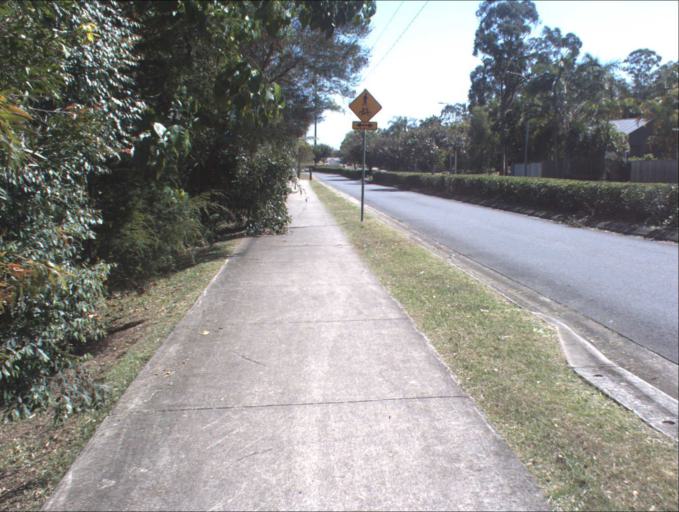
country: AU
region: Queensland
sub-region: Logan
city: Springwood
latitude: -27.6126
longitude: 153.1428
